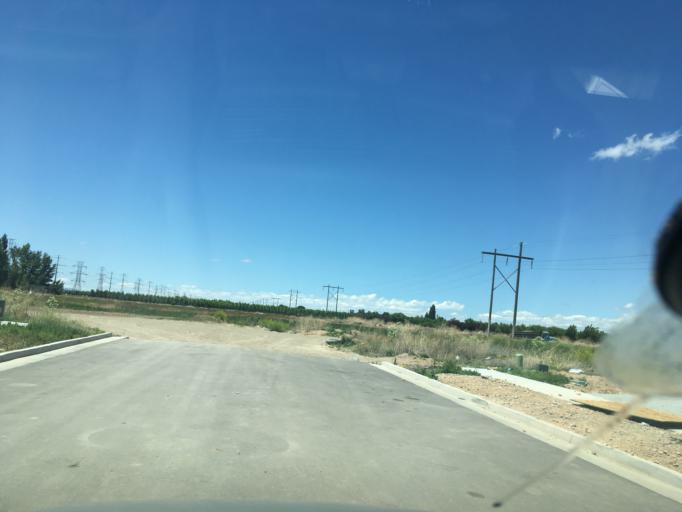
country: US
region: Utah
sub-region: Davis County
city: Layton
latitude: 41.0516
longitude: -111.9999
